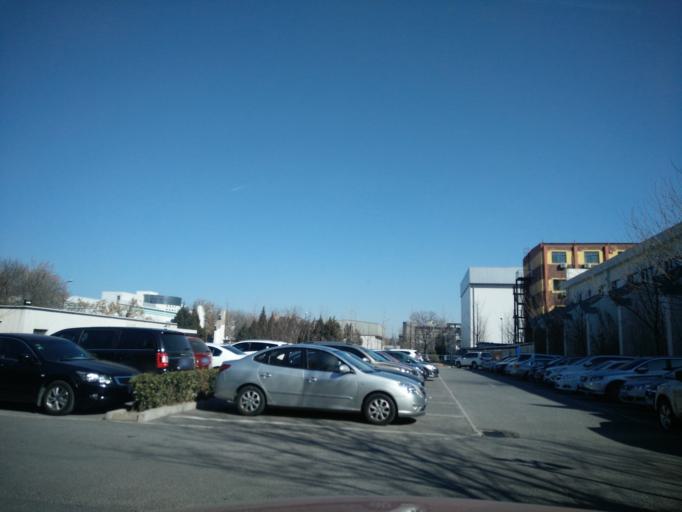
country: CN
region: Beijing
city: Jiugong
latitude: 39.7965
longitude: 116.5056
